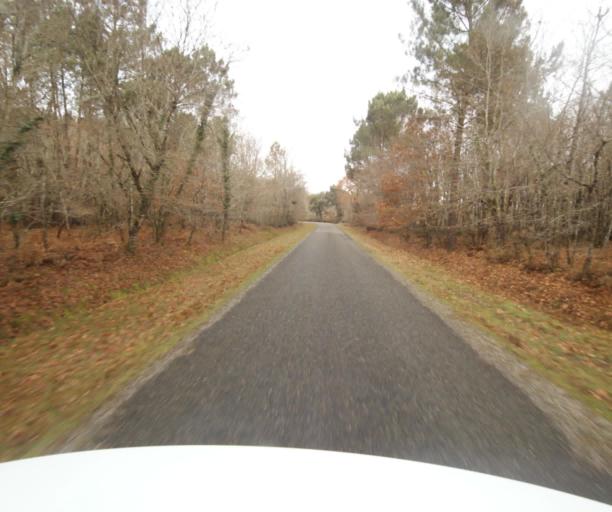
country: FR
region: Aquitaine
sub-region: Departement des Landes
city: Gabarret
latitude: 44.0919
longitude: 0.0658
